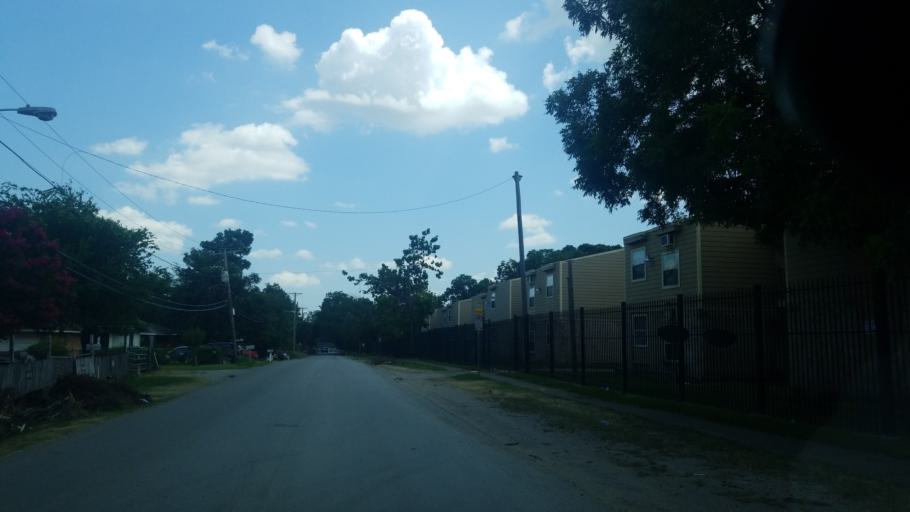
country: US
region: Texas
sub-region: Dallas County
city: Dallas
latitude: 32.7139
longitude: -96.7663
